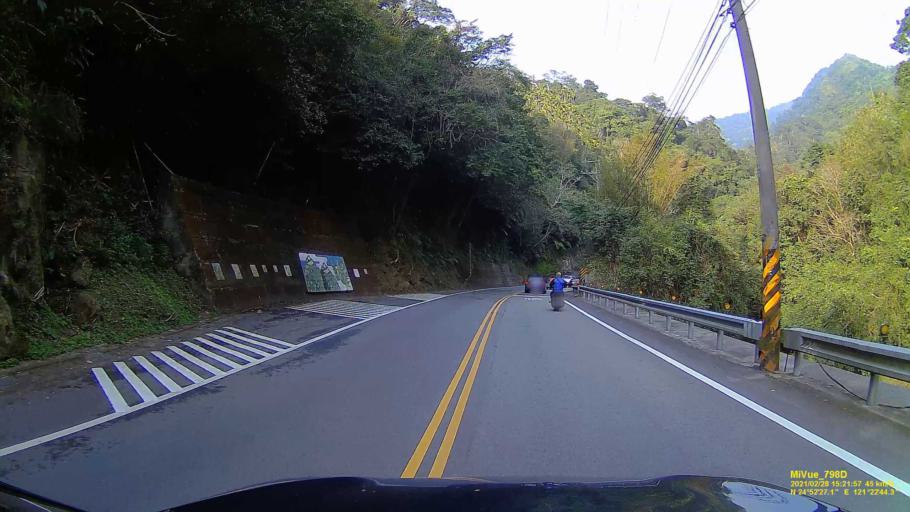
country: TW
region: Taiwan
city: Daxi
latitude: 24.8742
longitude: 121.3791
